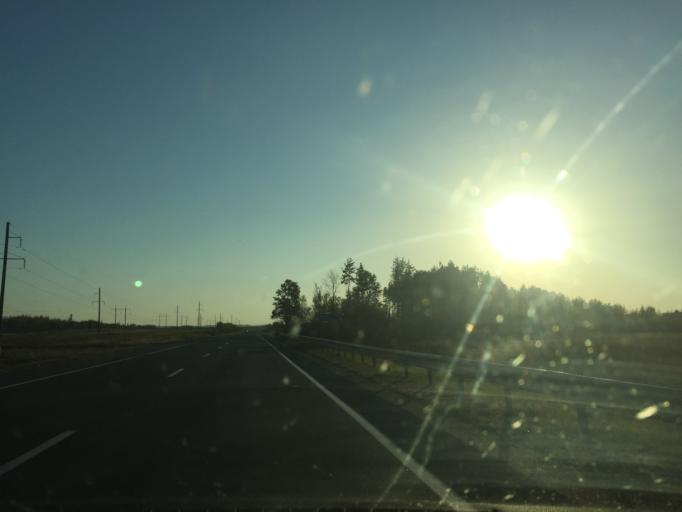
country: BY
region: Mogilev
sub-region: Mahilyowski Rayon
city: Veyno
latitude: 53.8063
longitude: 30.4504
